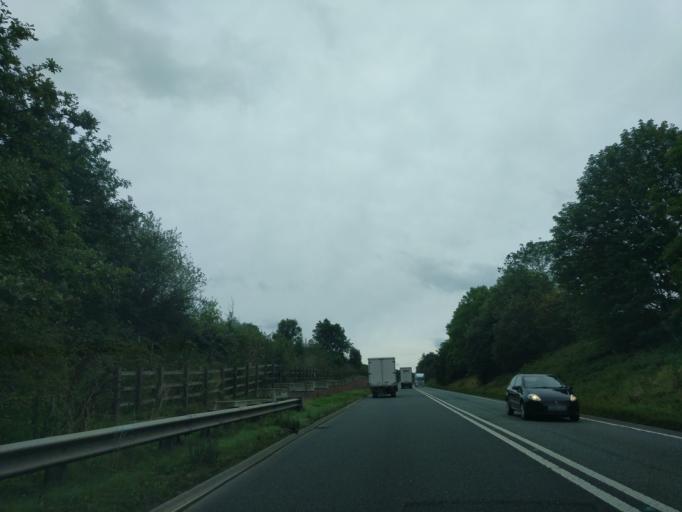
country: GB
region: England
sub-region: Cheshire East
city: Alsager
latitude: 53.0706
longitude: -2.3441
